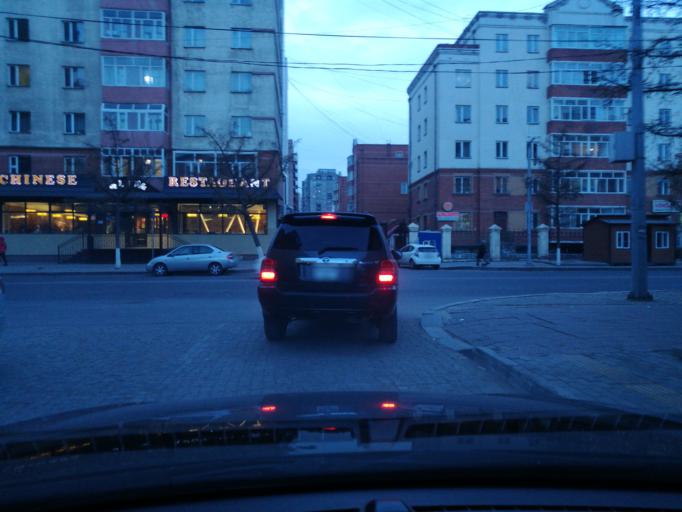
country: MN
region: Ulaanbaatar
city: Ulaanbaatar
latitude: 47.9277
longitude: 106.9178
